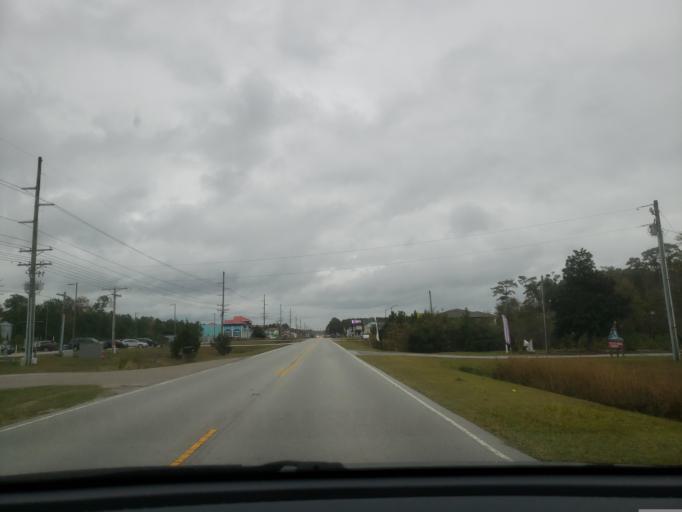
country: US
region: North Carolina
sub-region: Onslow County
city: Sneads Ferry
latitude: 34.5227
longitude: -77.4355
